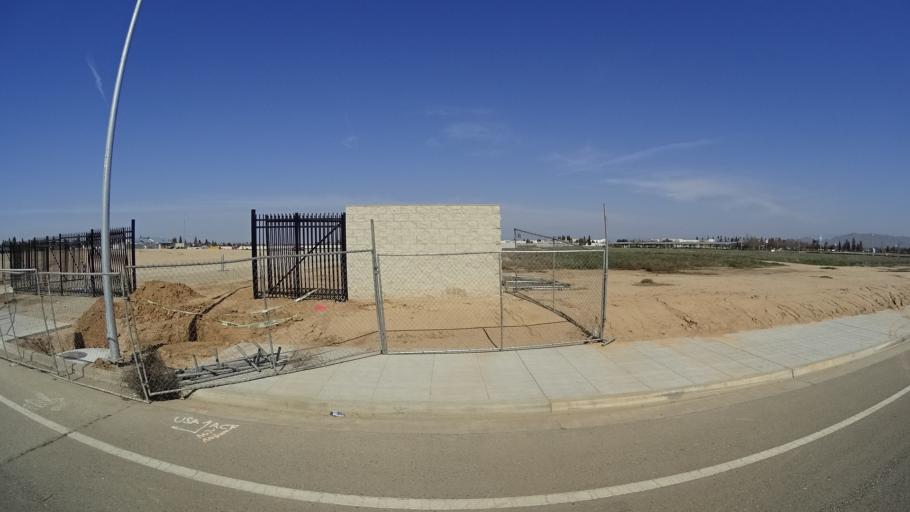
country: US
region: California
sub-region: Fresno County
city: Clovis
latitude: 36.8814
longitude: -119.7346
